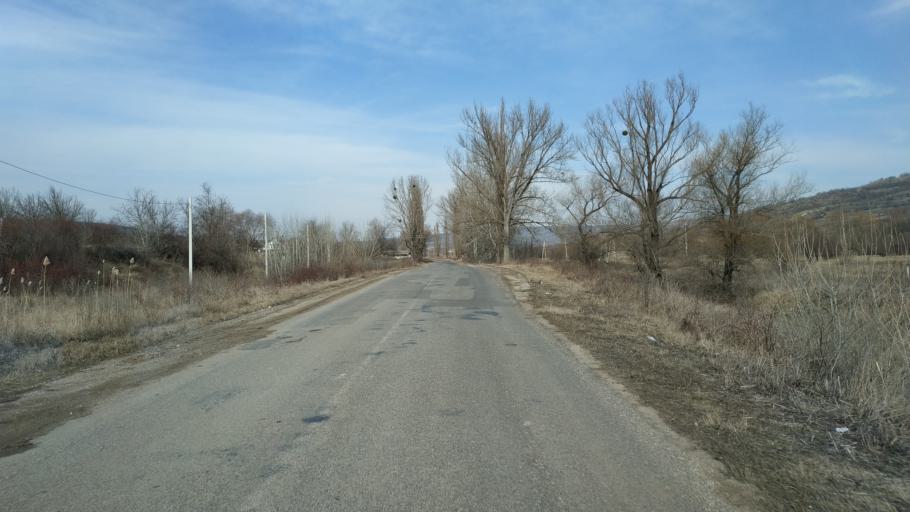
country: MD
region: Nisporeni
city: Nisporeni
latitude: 47.1578
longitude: 28.1059
